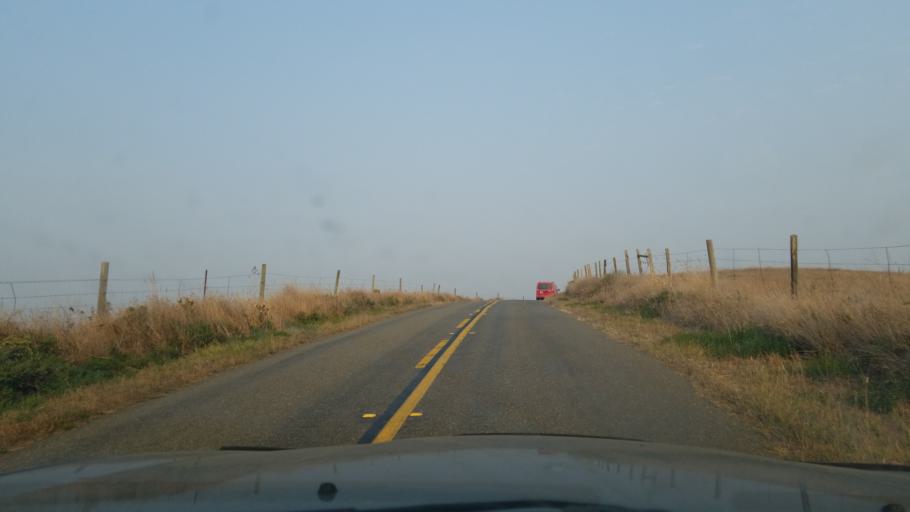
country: US
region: California
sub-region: Marin County
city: Inverness
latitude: 38.1215
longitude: -122.9308
